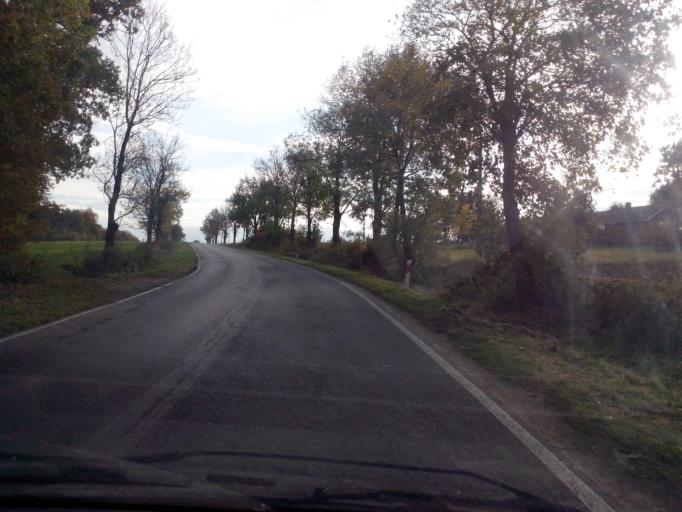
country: PL
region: Subcarpathian Voivodeship
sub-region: Powiat ropczycko-sedziszowski
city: Wielopole Skrzynskie
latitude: 49.9298
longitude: 21.6092
